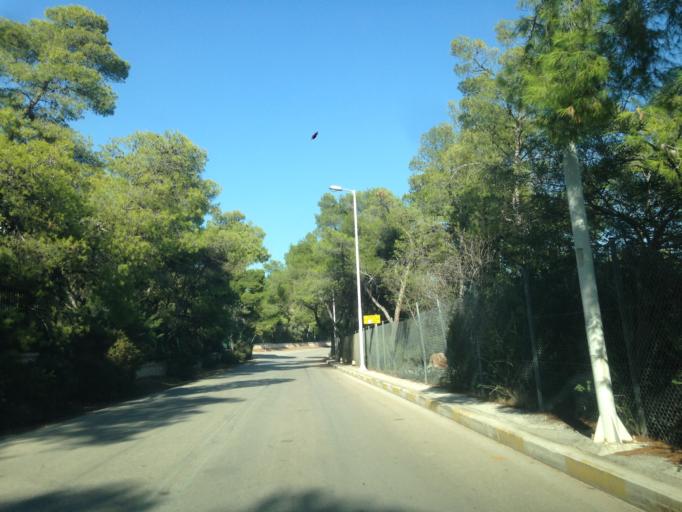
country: GR
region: Attica
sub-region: Nomarchia Anatolikis Attikis
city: Vouliagmeni
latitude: 37.8038
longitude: 23.7718
